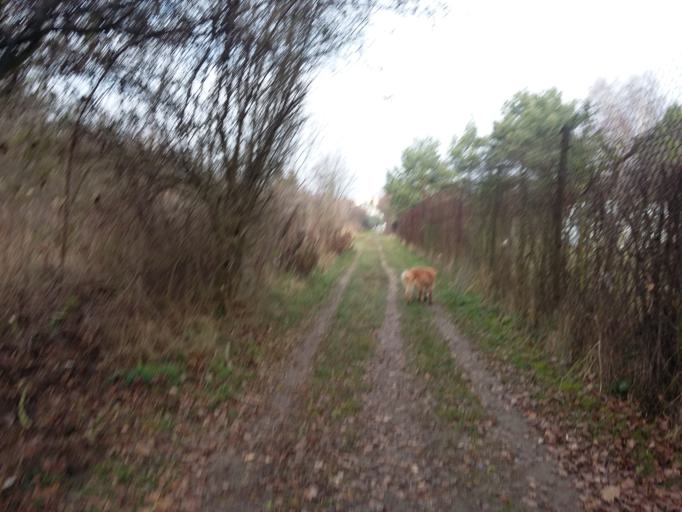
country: PL
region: Lodz Voivodeship
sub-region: Powiat pabianicki
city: Ksawerow
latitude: 51.7364
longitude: 19.4119
